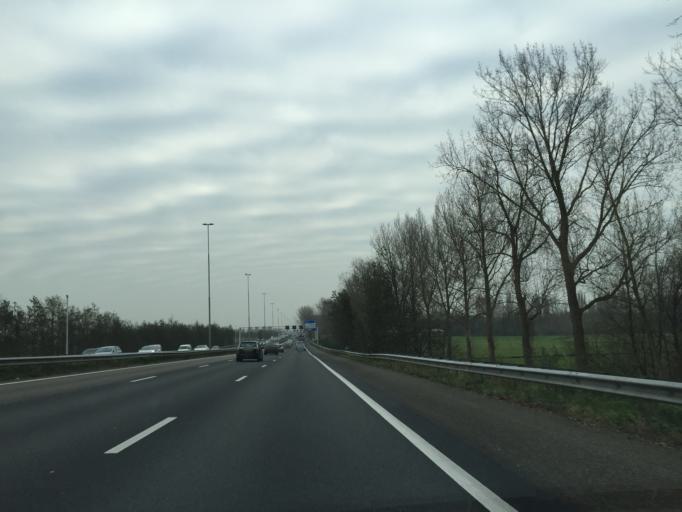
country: NL
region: South Holland
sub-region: Gemeente Schiedam
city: Schiedam
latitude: 51.9659
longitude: 4.4038
